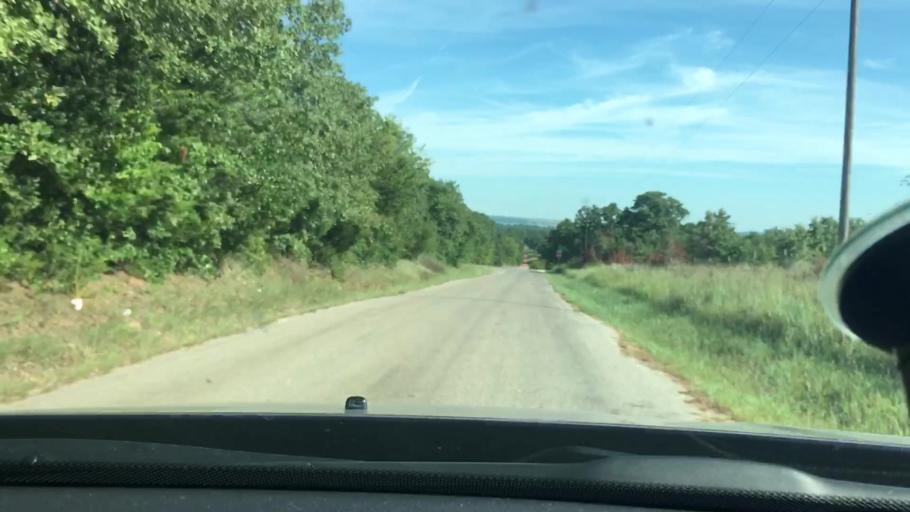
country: US
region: Oklahoma
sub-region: Carter County
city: Lone Grove
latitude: 34.2660
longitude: -97.2474
